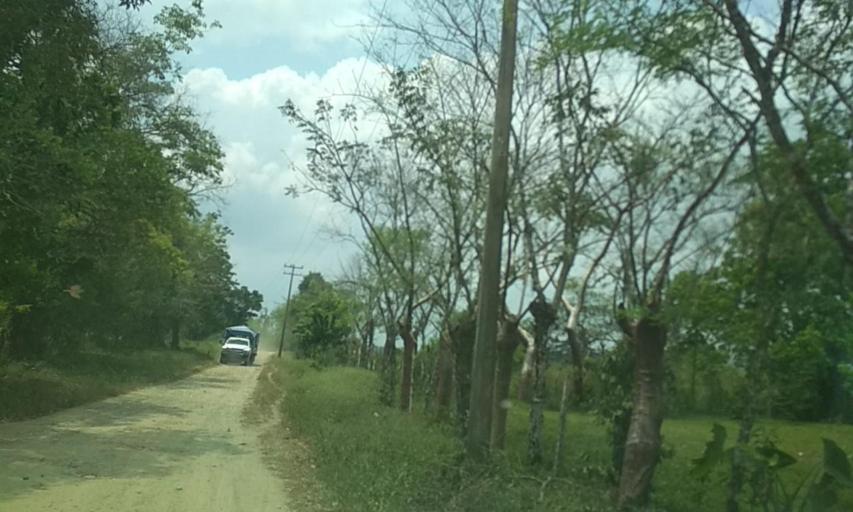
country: MX
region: Tabasco
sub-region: Huimanguillo
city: Francisco Rueda
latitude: 17.5807
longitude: -93.7899
